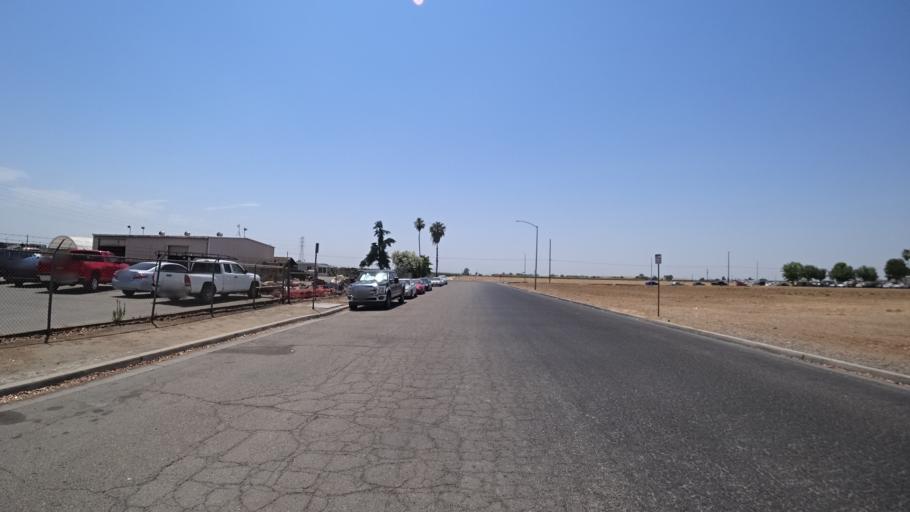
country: US
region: California
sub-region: Fresno County
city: West Park
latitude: 36.7151
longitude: -119.8225
